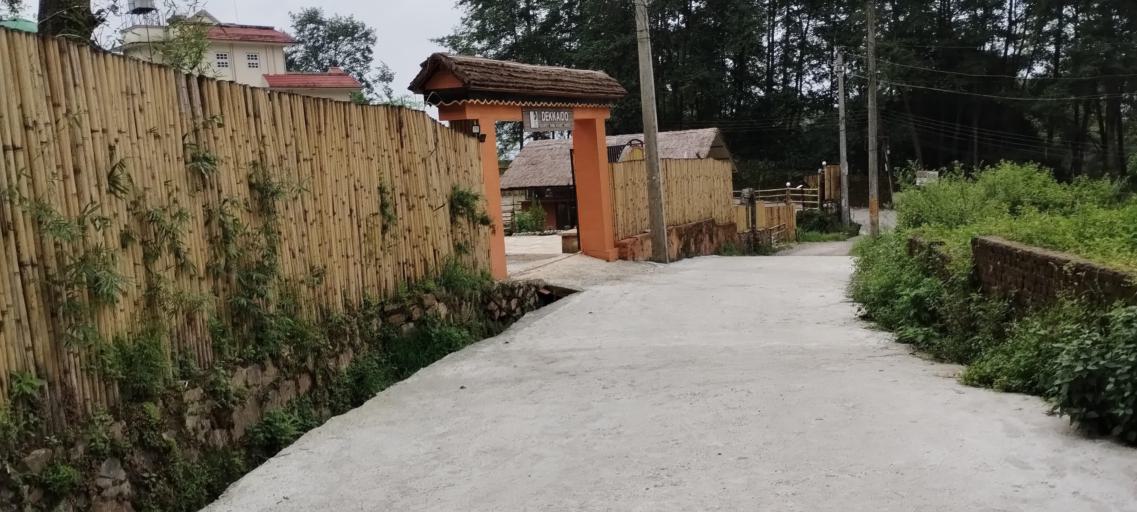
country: NP
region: Central Region
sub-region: Bagmati Zone
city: Kathmandu
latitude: 27.7851
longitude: 85.3606
